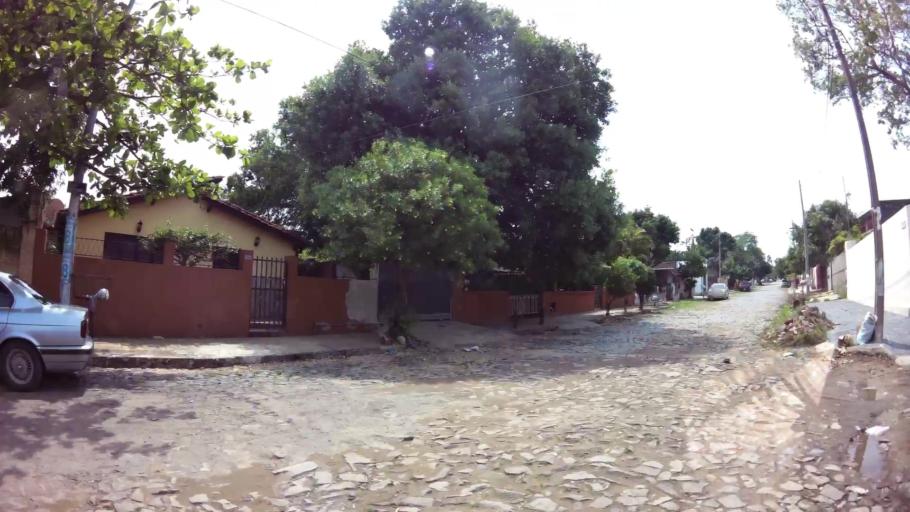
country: PY
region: Asuncion
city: Asuncion
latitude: -25.2657
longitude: -57.5860
